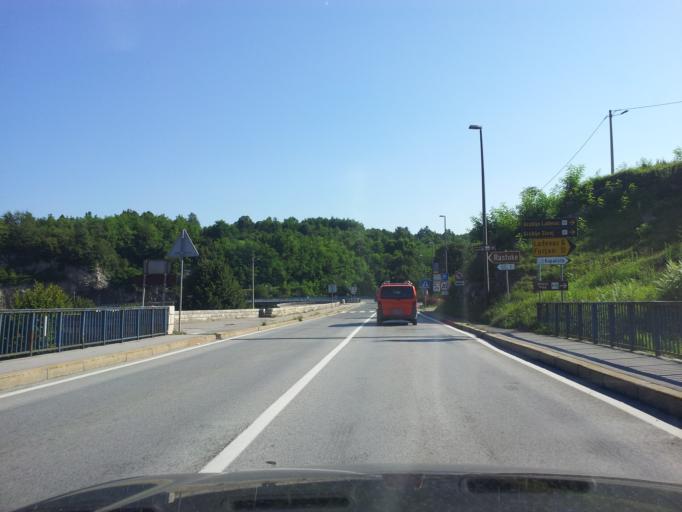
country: HR
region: Karlovacka
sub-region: Grad Karlovac
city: Slunj
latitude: 45.1199
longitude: 15.5873
